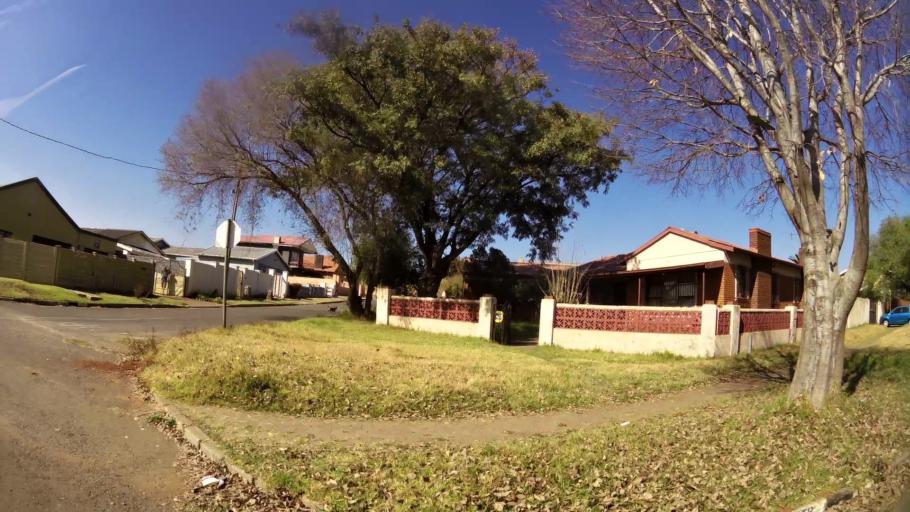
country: ZA
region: Gauteng
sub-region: City of Johannesburg Metropolitan Municipality
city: Roodepoort
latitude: -26.1969
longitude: 27.9530
